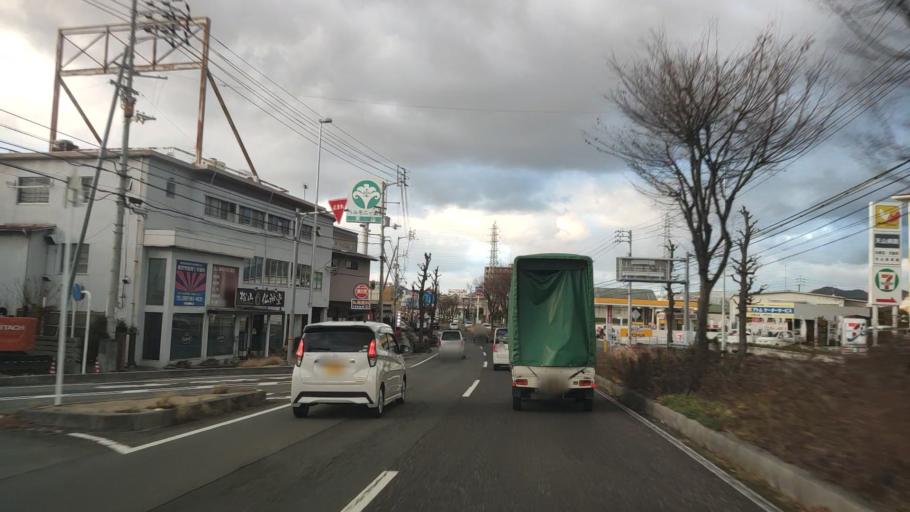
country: JP
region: Ehime
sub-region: Shikoku-chuo Shi
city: Matsuyama
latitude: 33.8184
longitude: 132.7770
